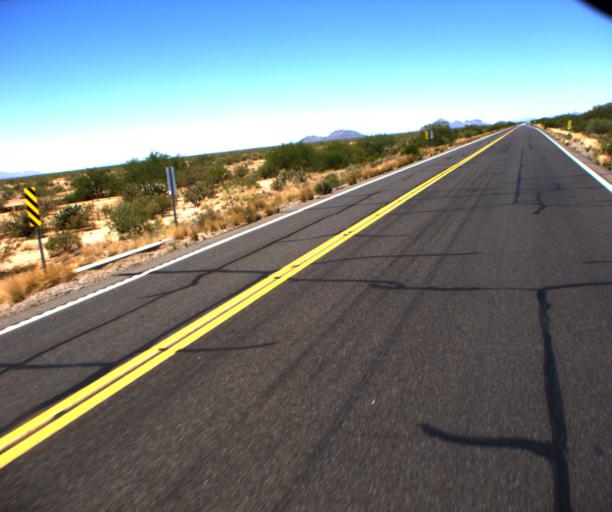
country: US
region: Arizona
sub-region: Yavapai County
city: Congress
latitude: 34.1374
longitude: -112.9706
